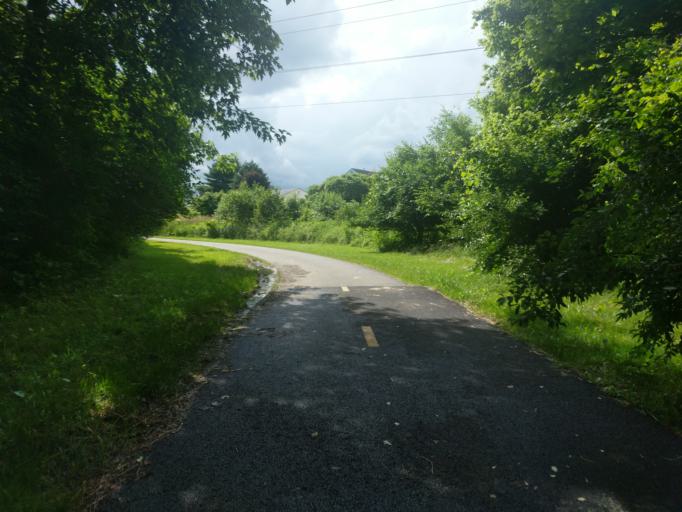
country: US
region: Ohio
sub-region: Franklin County
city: Minerva Park
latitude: 40.0658
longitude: -82.9238
